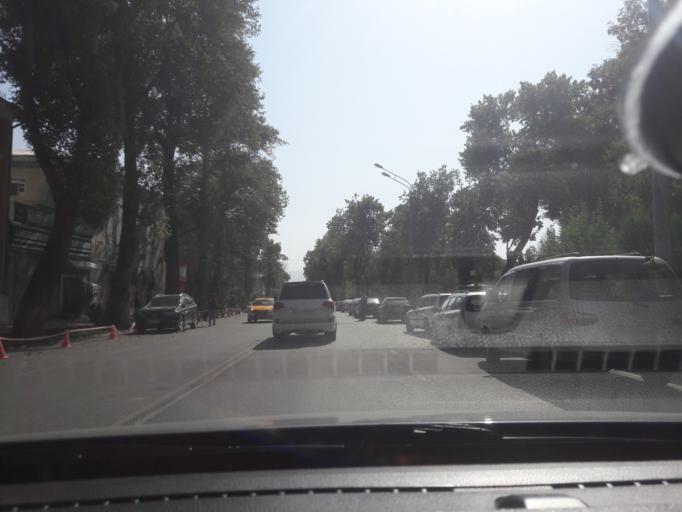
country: TJ
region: Dushanbe
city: Dushanbe
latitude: 38.5716
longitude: 68.7999
